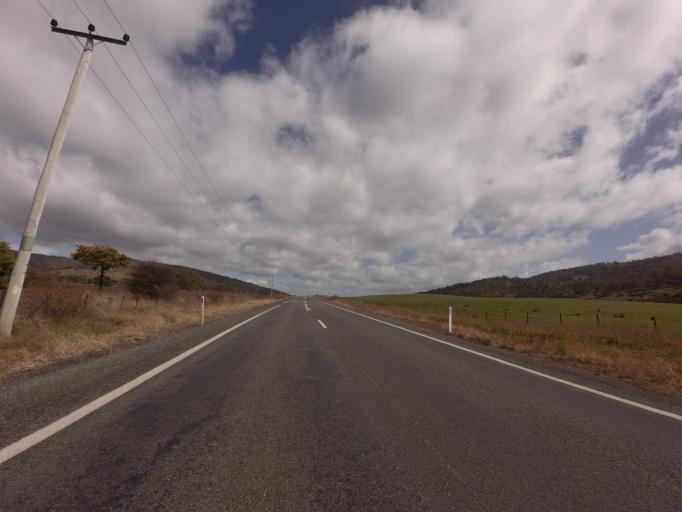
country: AU
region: Tasmania
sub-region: Northern Midlands
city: Evandale
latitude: -41.8116
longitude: 147.5890
